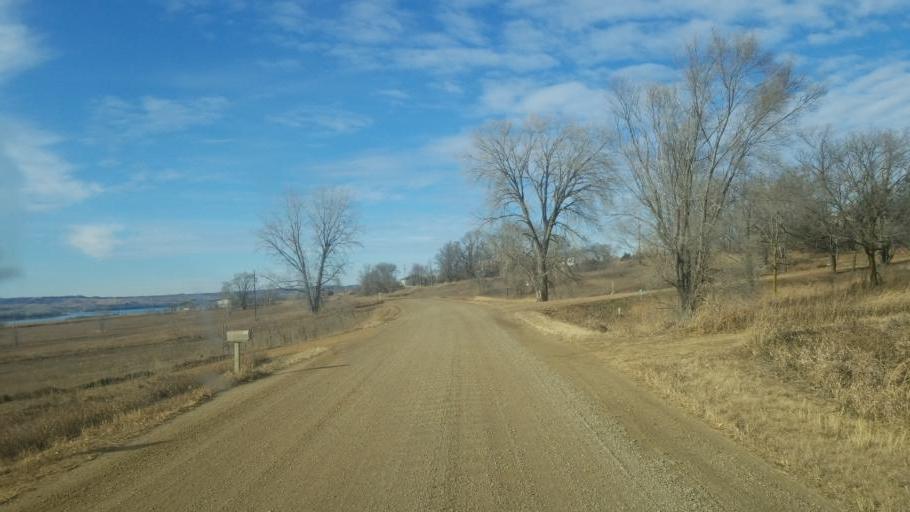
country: US
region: South Dakota
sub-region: Charles Mix County
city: Wagner
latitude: 42.9257
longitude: -98.3931
